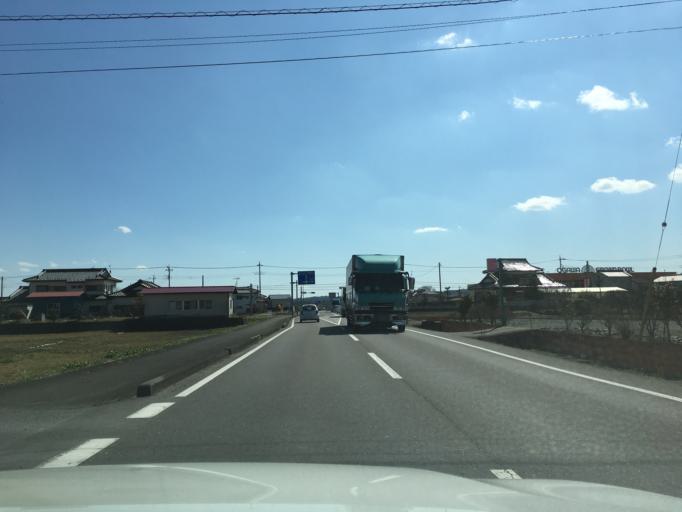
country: JP
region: Tochigi
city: Karasuyama
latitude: 36.7595
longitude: 140.1363
